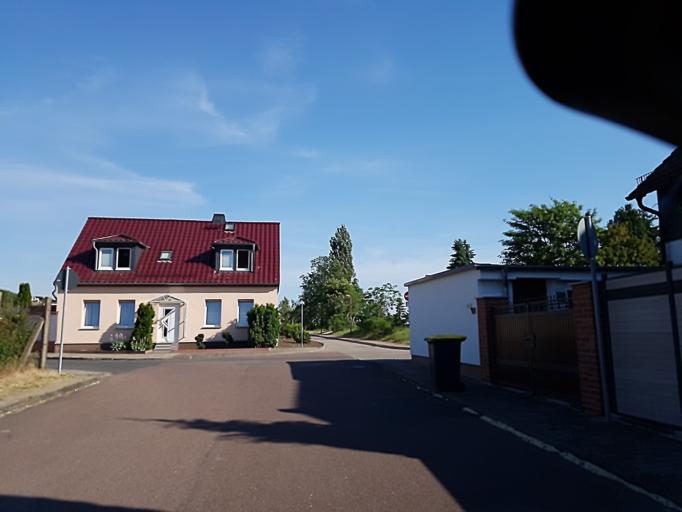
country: DE
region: Saxony-Anhalt
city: Coswig
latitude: 51.8889
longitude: 12.4555
